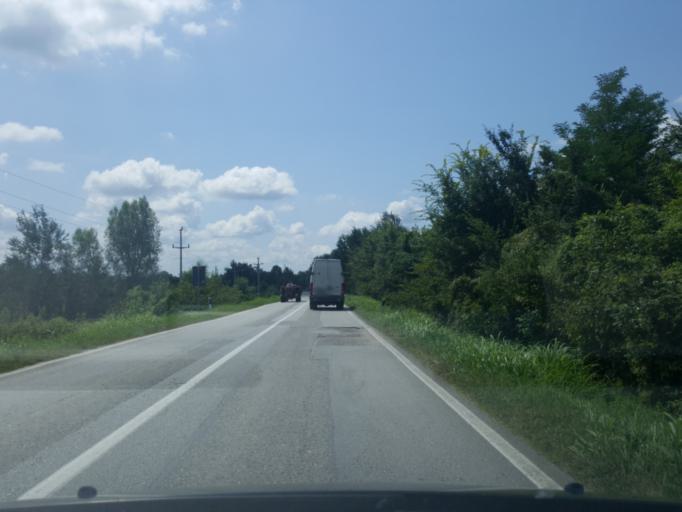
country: RS
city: Glusci
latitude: 44.9231
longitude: 19.5440
